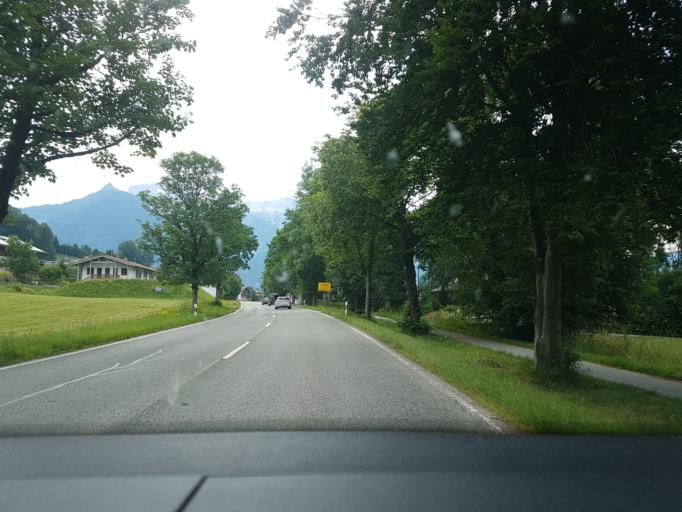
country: DE
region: Bavaria
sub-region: Upper Bavaria
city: Berchtesgaden
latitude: 47.6354
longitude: 12.9765
